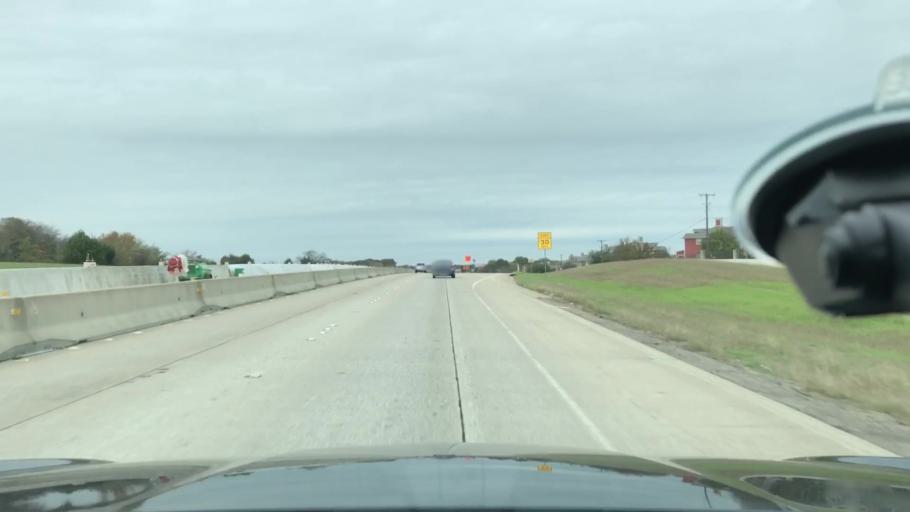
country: US
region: Texas
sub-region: Ellis County
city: Waxahachie
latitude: 32.3900
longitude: -96.8690
